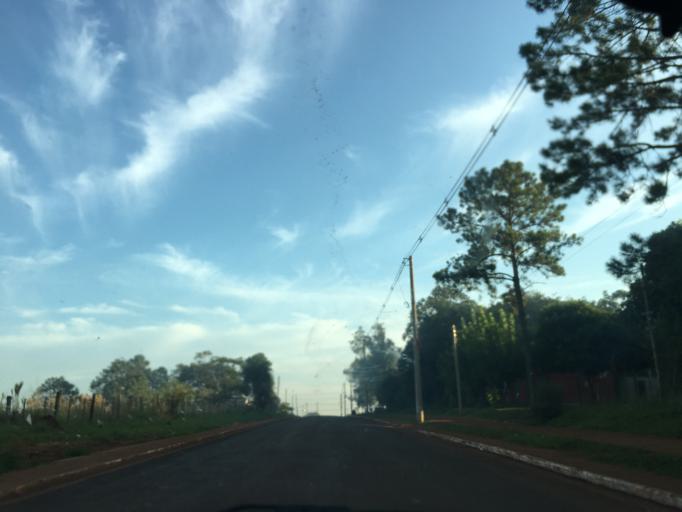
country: AR
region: Misiones
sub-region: Departamento de Capital
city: Posadas
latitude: -27.4459
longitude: -55.9333
